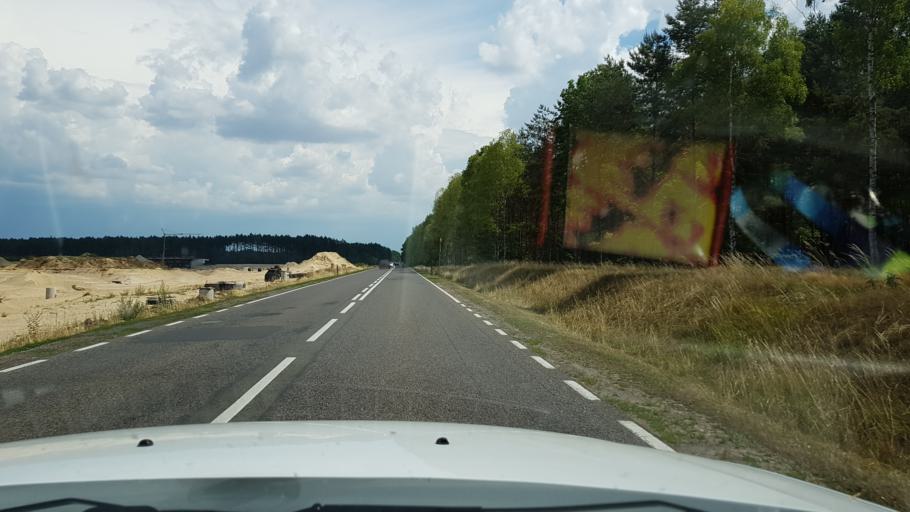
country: PL
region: West Pomeranian Voivodeship
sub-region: Powiat walecki
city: Walcz
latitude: 53.2979
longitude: 16.4186
